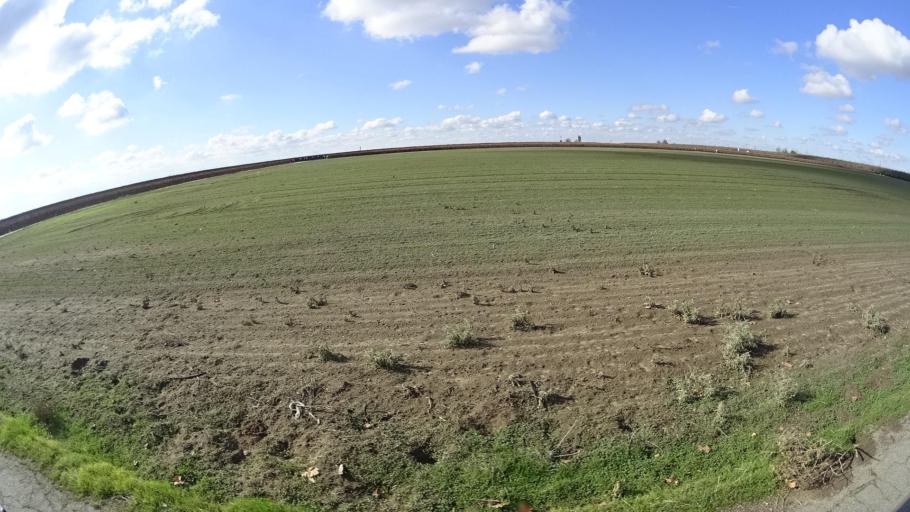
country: US
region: California
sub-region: Kern County
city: Delano
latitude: 35.7365
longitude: -119.3480
